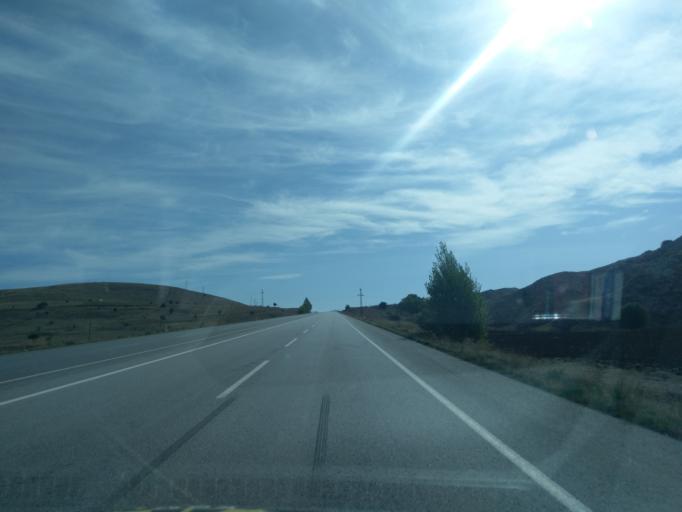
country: TR
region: Sivas
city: Imranli
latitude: 39.8842
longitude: 38.0386
